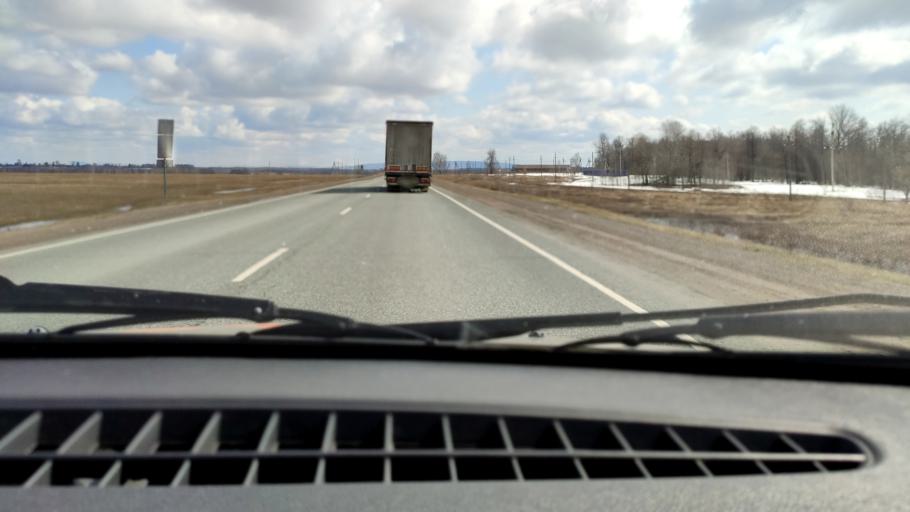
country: RU
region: Bashkortostan
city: Kudeyevskiy
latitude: 54.8168
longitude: 56.7454
